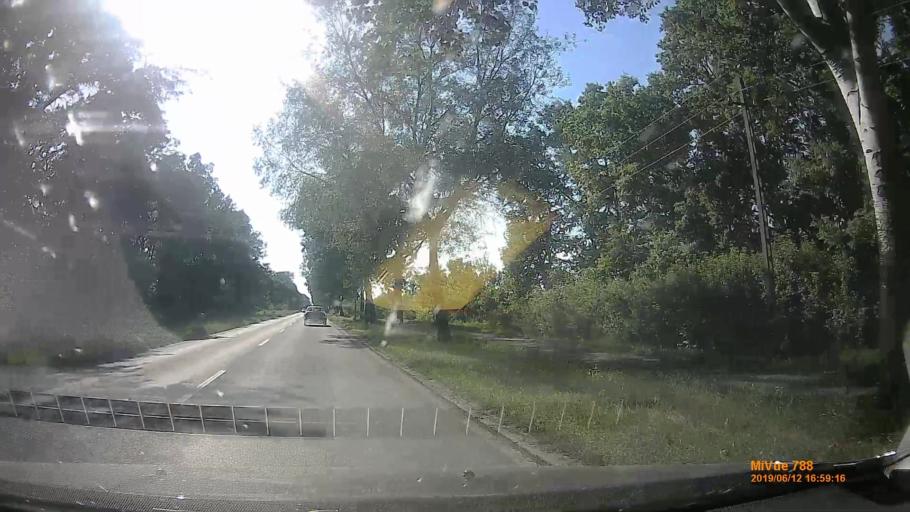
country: HU
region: Csongrad
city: Deszk
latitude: 46.2178
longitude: 20.2688
